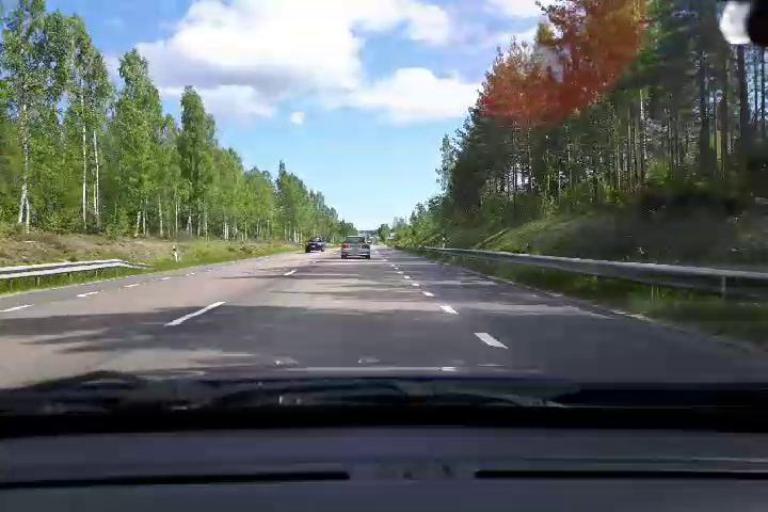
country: SE
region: Gaevleborg
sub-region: Hudiksvalls Kommun
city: Sorforsa
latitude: 61.7186
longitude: 17.0268
